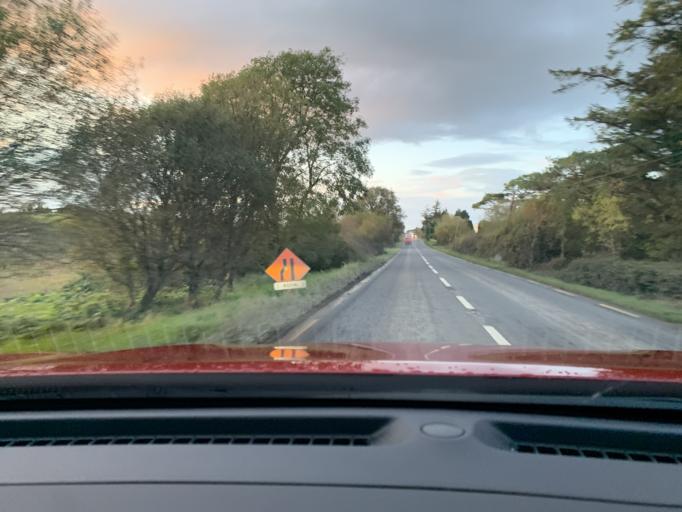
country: IE
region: Connaught
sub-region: Sligo
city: Collooney
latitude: 54.1483
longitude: -8.4625
